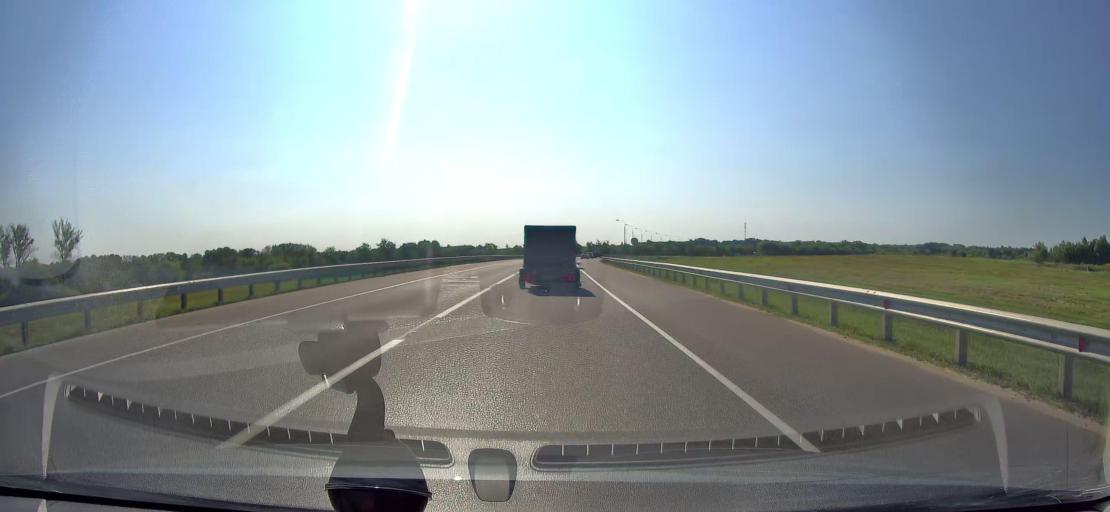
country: RU
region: Orjol
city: Kromy
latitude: 52.6485
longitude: 35.7397
